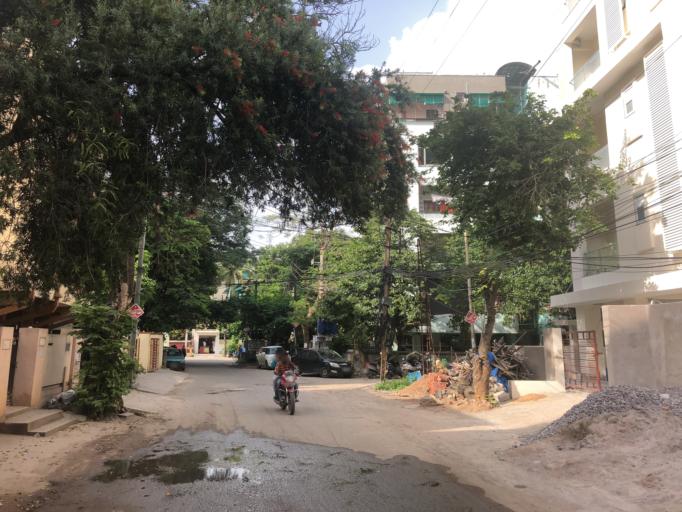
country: IN
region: Telangana
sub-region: Rangareddi
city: Kukatpalli
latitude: 17.4388
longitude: 78.4331
